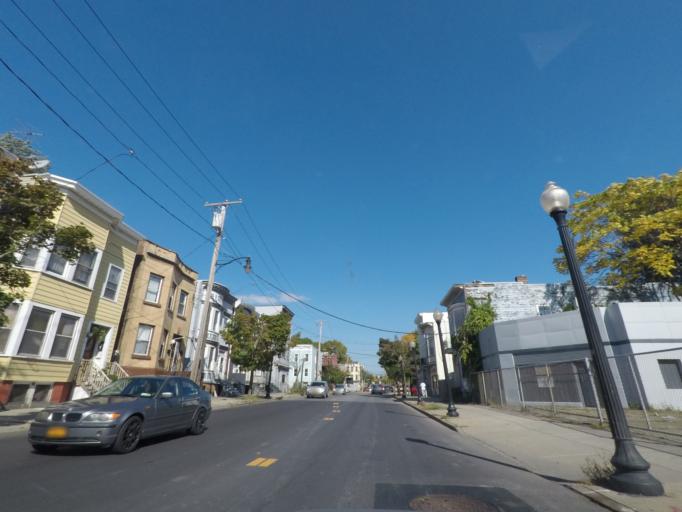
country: US
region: New York
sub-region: Albany County
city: Albany
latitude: 42.6600
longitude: -73.7627
